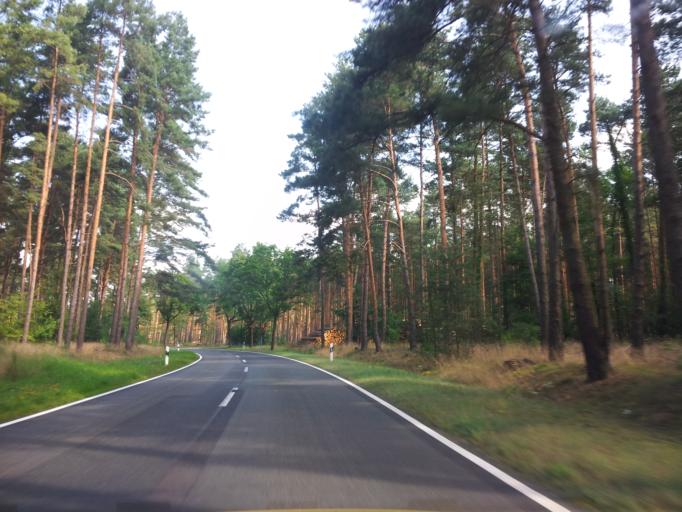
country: DE
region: Brandenburg
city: Niedergorsdorf
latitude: 52.0387
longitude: 12.9427
